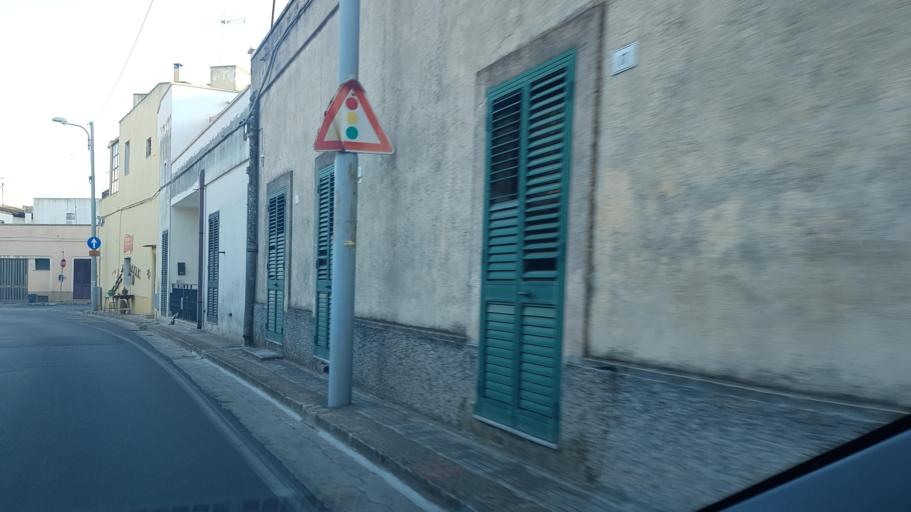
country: IT
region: Apulia
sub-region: Provincia di Lecce
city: Lucugnano
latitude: 39.9352
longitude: 18.3192
